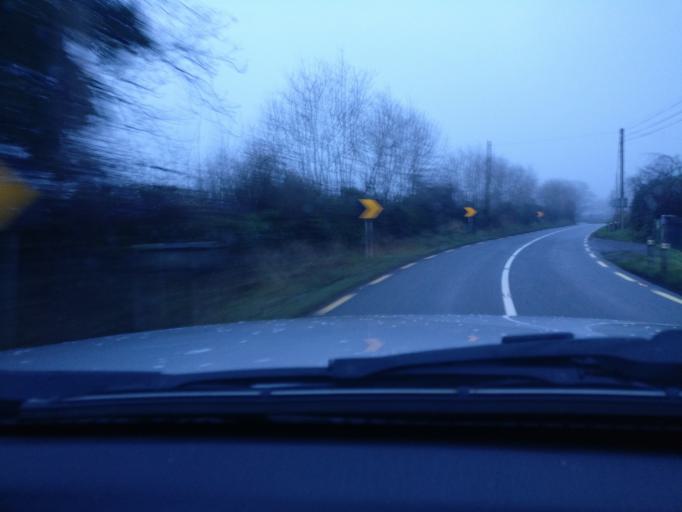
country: IE
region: Leinster
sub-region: An Mhi
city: Athboy
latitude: 53.6131
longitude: -6.9448
